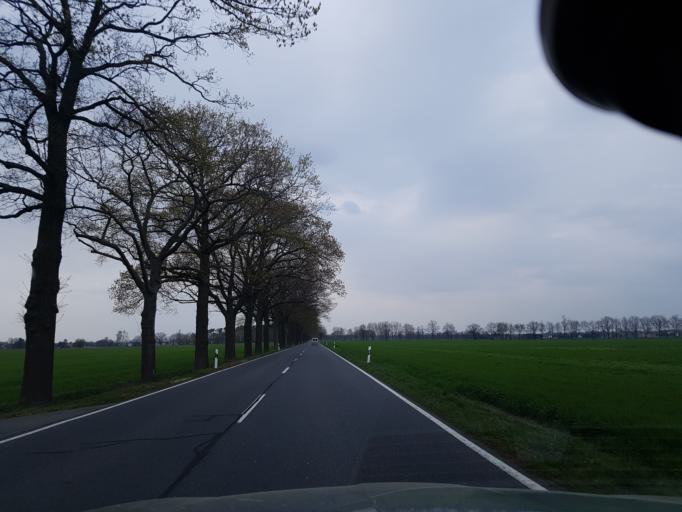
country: DE
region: Brandenburg
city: Schraden
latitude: 51.4127
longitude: 13.6987
